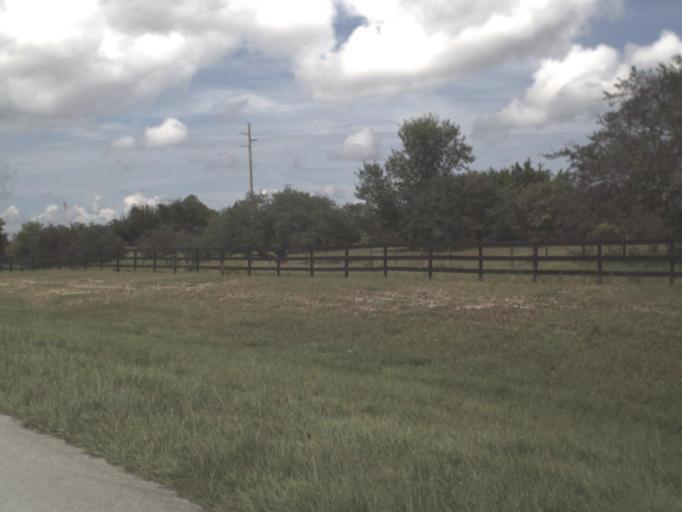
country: US
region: Florida
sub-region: Highlands County
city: Lake Placid
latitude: 27.2083
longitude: -81.2961
